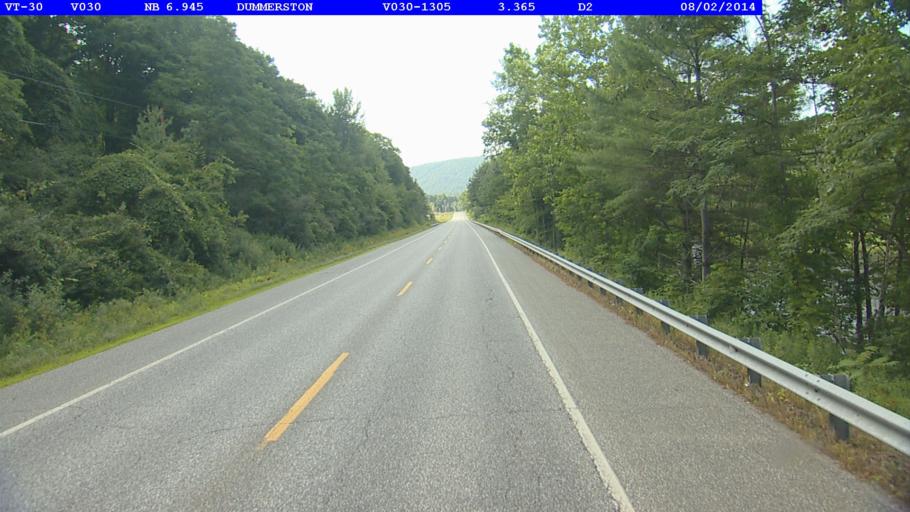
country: US
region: Vermont
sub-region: Windham County
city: Newfane
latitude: 42.9406
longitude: -72.6154
